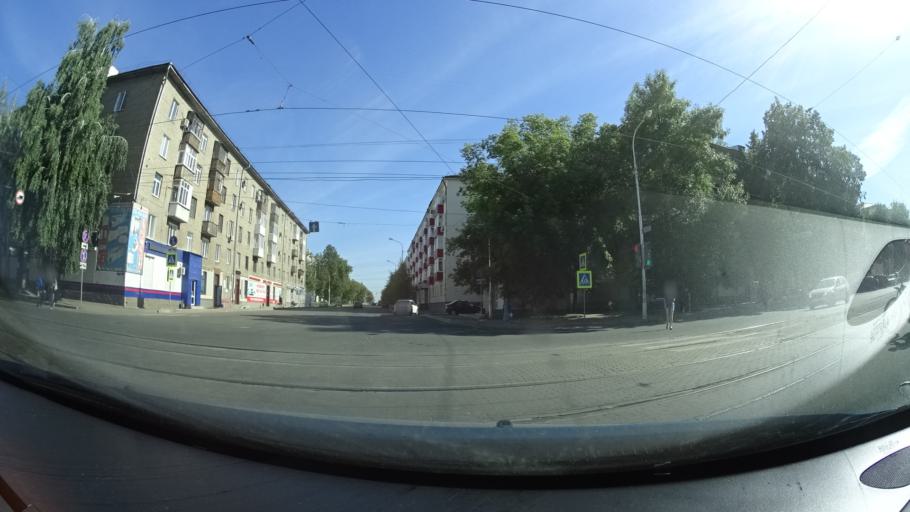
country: RU
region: Bashkortostan
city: Ufa
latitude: 54.7337
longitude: 55.9640
